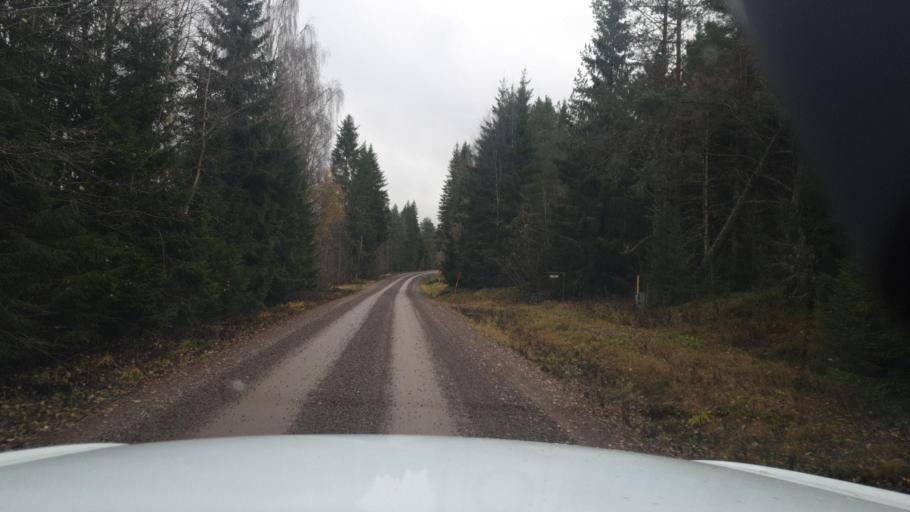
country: SE
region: Vaermland
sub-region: Eda Kommun
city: Charlottenberg
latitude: 60.0842
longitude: 12.5202
